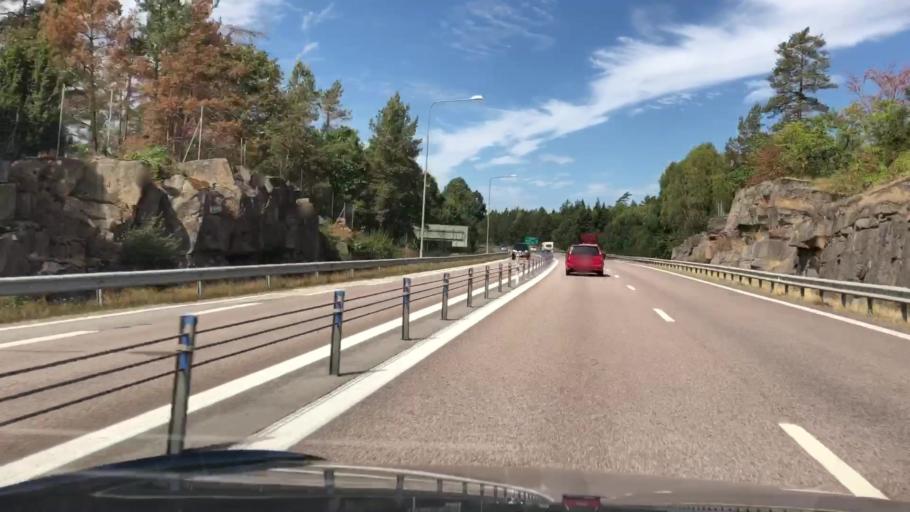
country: SE
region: Blekinge
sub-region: Ronneby Kommun
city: Kallinge
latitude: 56.2103
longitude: 15.3216
